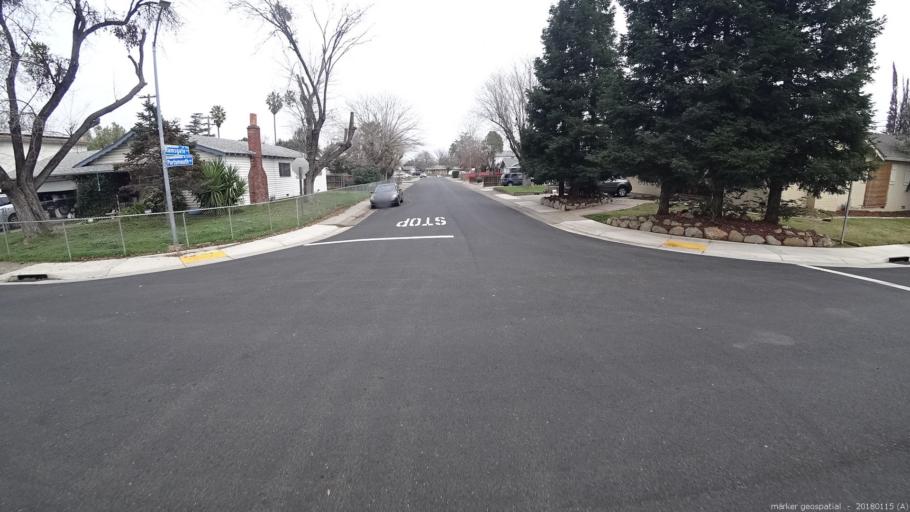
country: US
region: California
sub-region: Sacramento County
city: Rancho Cordova
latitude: 38.5813
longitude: -121.3070
